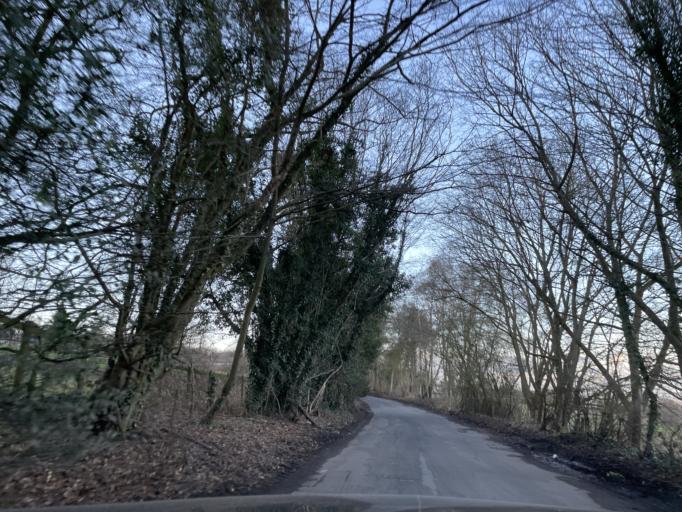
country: GB
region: England
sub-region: Kent
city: Westerham
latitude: 51.2582
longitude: 0.1224
